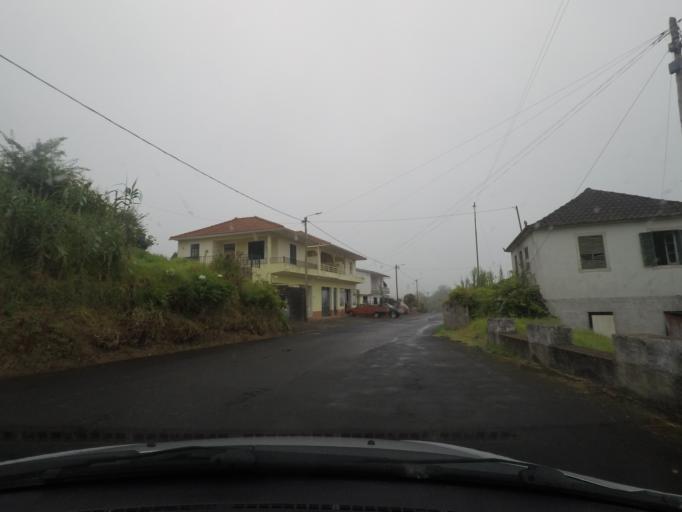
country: PT
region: Madeira
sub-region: Santana
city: Santana
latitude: 32.7941
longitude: -16.8727
